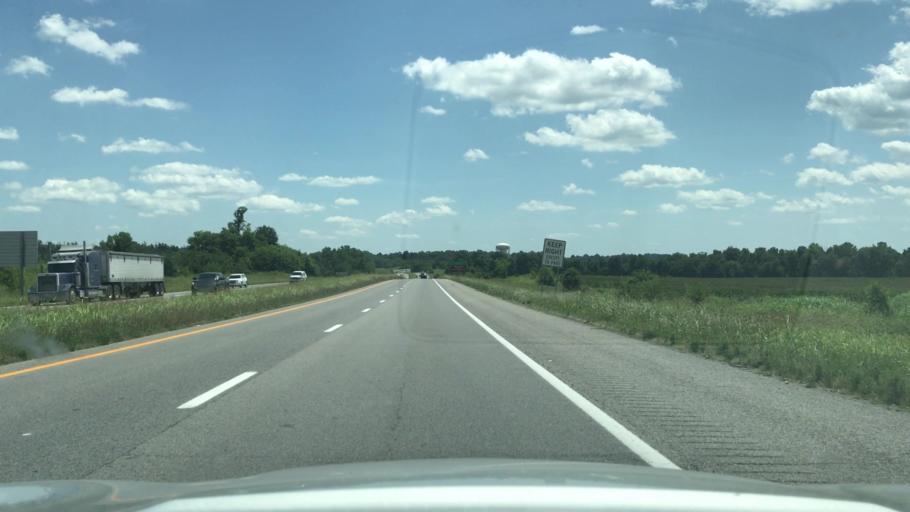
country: US
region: Kentucky
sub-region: Christian County
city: Hopkinsville
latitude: 36.8879
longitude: -87.4692
